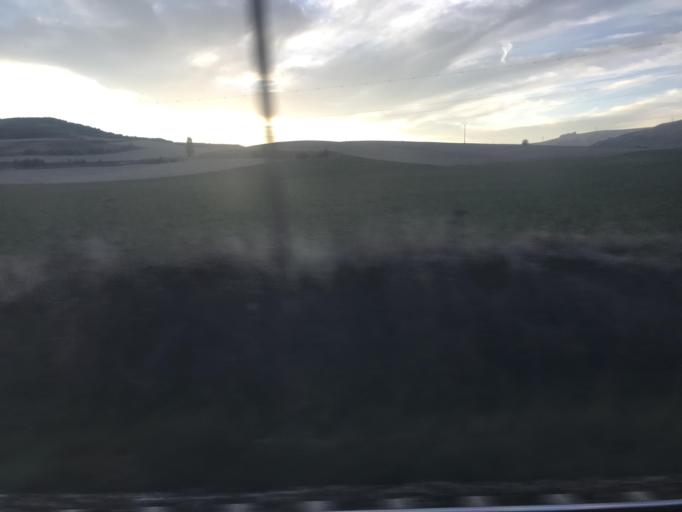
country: ES
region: Castille and Leon
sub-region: Provincia de Burgos
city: Monasterio de Rodilla
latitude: 42.4538
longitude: -3.4522
